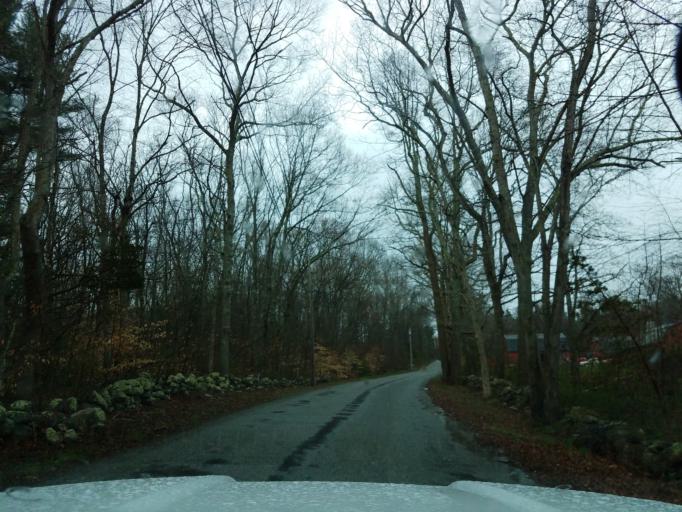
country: US
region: Rhode Island
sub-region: Washington County
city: Ashaway
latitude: 41.4456
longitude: -71.8205
